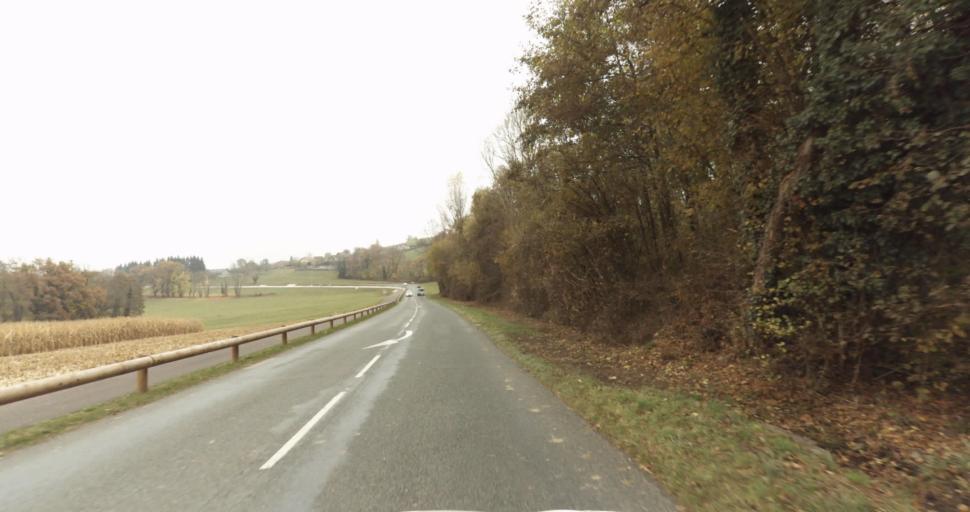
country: FR
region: Rhone-Alpes
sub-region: Departement de la Haute-Savoie
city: Alby-sur-Cheran
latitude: 45.8034
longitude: 6.0106
